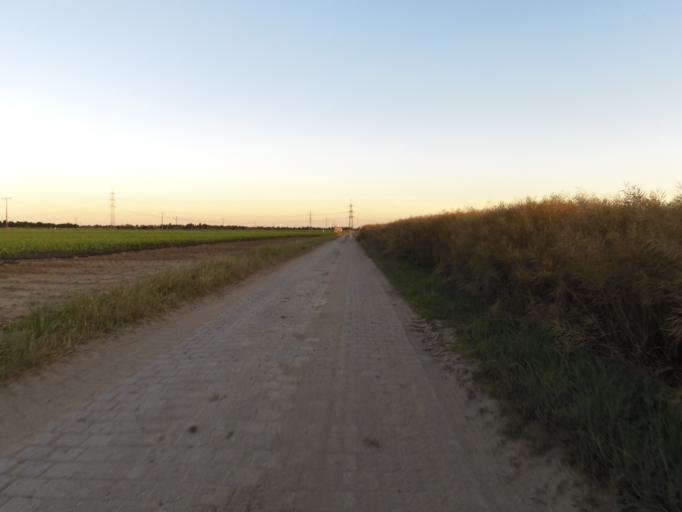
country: DE
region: Rheinland-Pfalz
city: Bobenheim-Roxheim
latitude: 49.5682
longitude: 8.3466
